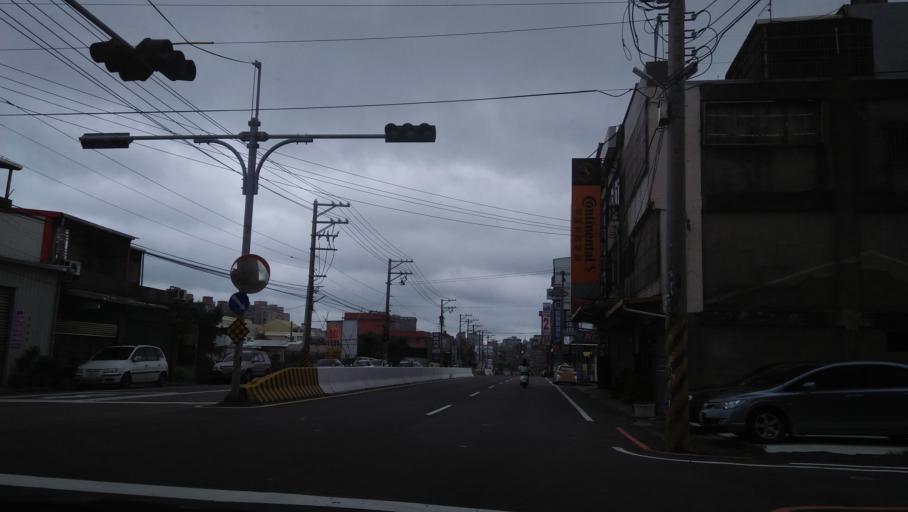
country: TW
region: Taiwan
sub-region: Hsinchu
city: Zhubei
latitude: 24.7779
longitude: 121.0329
